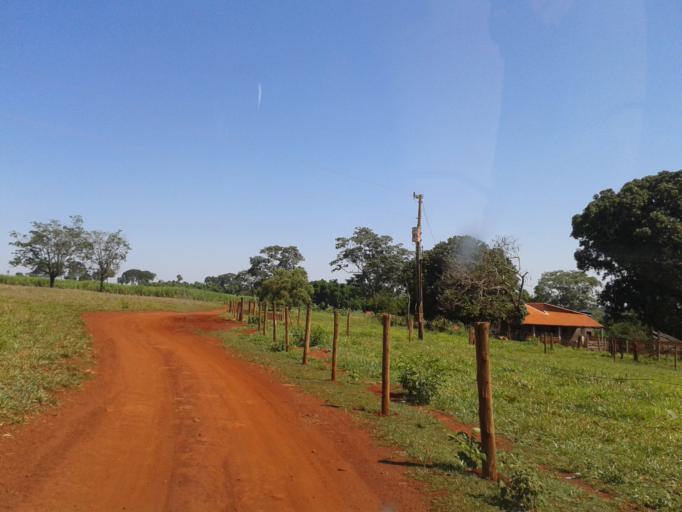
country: BR
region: Minas Gerais
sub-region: Centralina
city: Centralina
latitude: -18.6395
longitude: -49.2977
